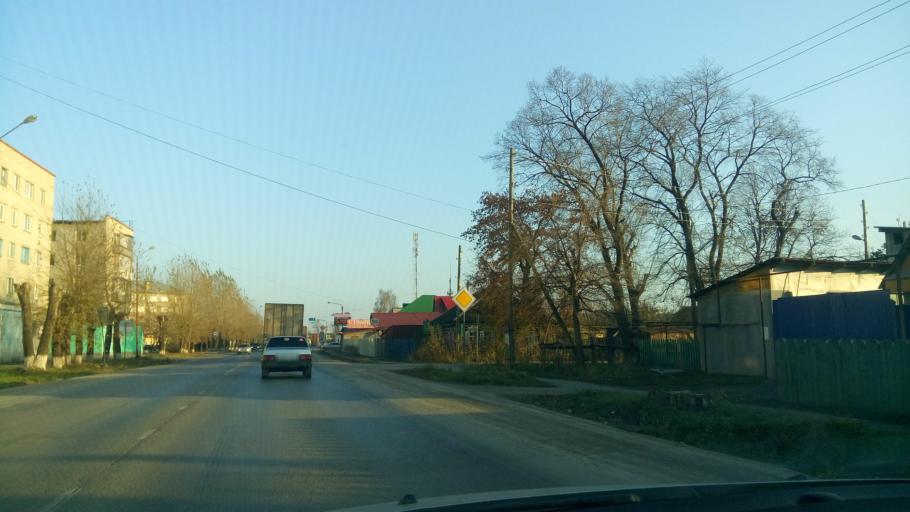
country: RU
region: Sverdlovsk
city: Bogdanovich
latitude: 56.7690
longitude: 62.0494
